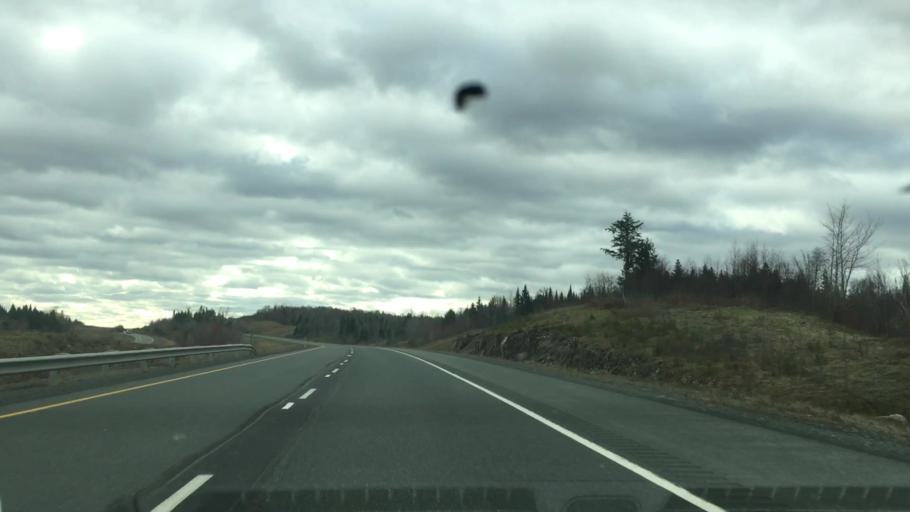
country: US
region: Maine
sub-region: Aroostook County
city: Fort Fairfield
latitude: 46.6425
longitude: -67.7444
